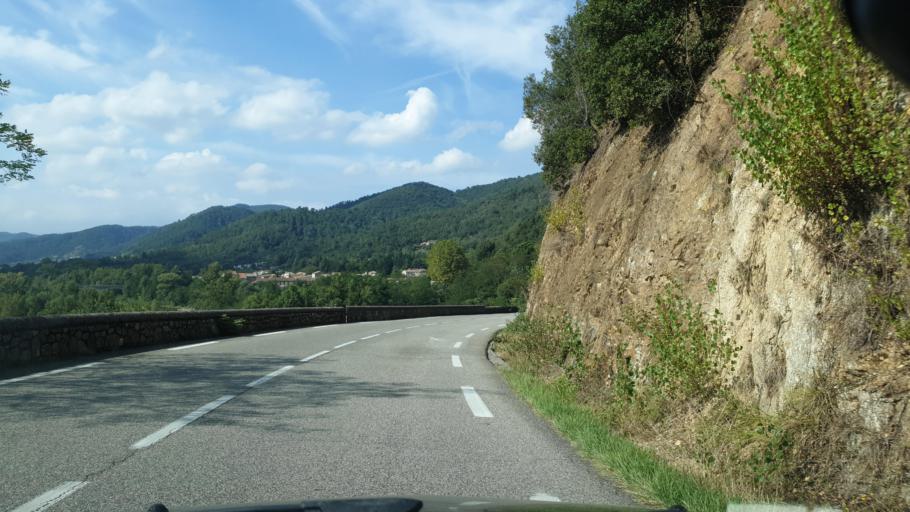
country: FR
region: Rhone-Alpes
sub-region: Departement de l'Ardeche
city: Saint-Laurent-du-Pape
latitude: 44.8292
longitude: 4.6859
